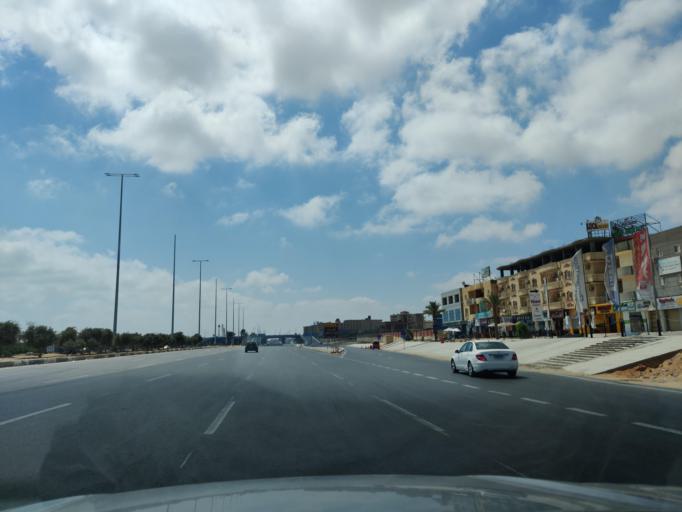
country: EG
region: Muhafazat Matruh
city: Al `Alamayn
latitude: 30.8423
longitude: 28.9474
